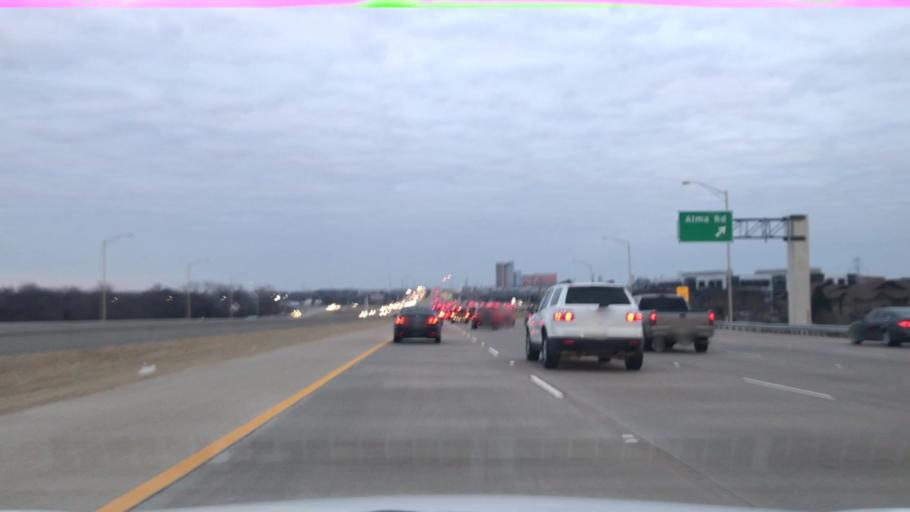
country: US
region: Texas
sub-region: Collin County
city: Plano
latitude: 33.0038
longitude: -96.7307
